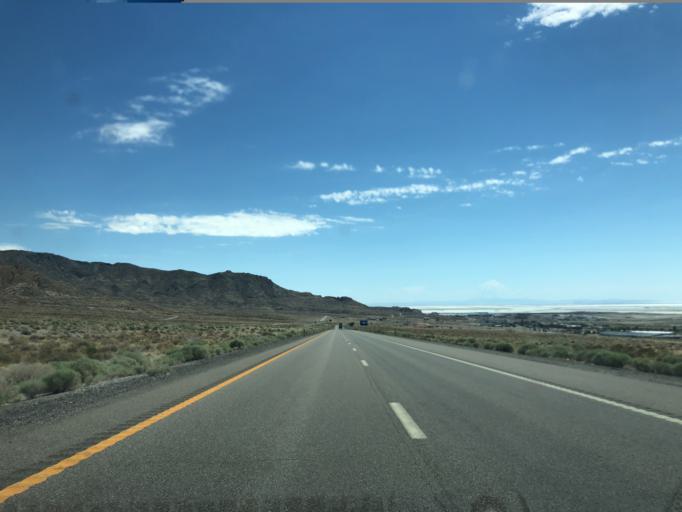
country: US
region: Nevada
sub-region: Elko County
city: West Wendover
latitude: 40.7441
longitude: -114.0903
